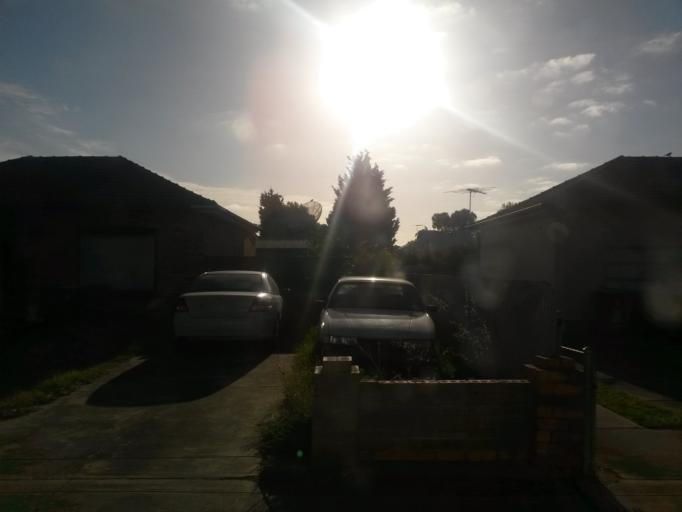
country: AU
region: South Australia
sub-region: Prospect
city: Prospect
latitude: -34.8879
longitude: 138.5762
